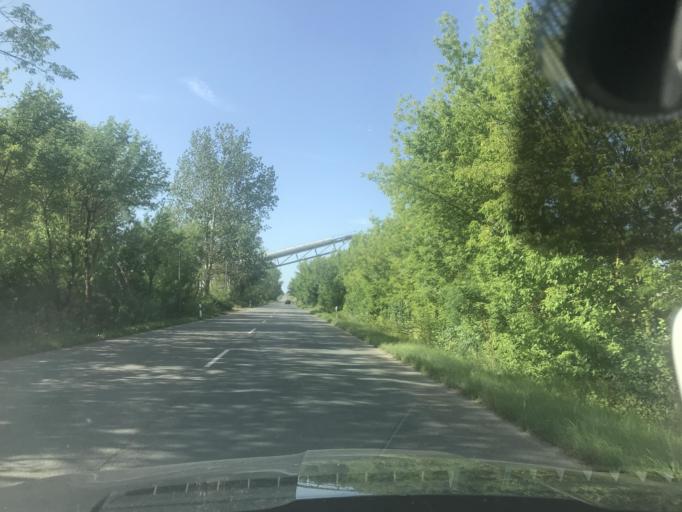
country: DE
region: Saxony-Anhalt
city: Wegeleben
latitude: 51.9081
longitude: 11.1492
